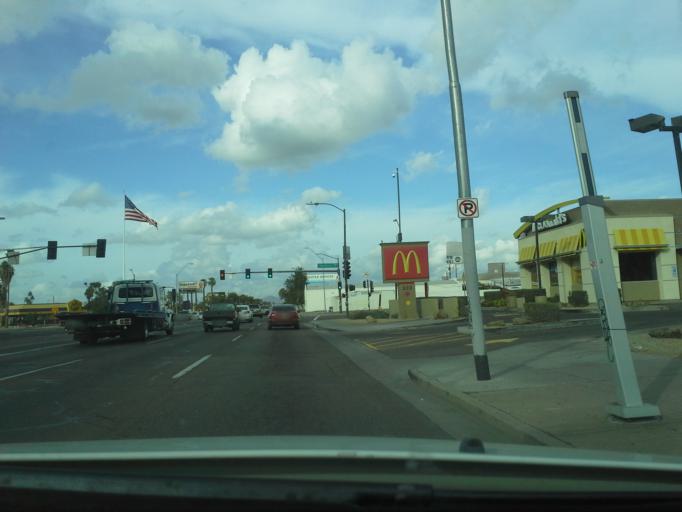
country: US
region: Arizona
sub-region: Maricopa County
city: Phoenix
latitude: 33.4508
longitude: -112.0825
